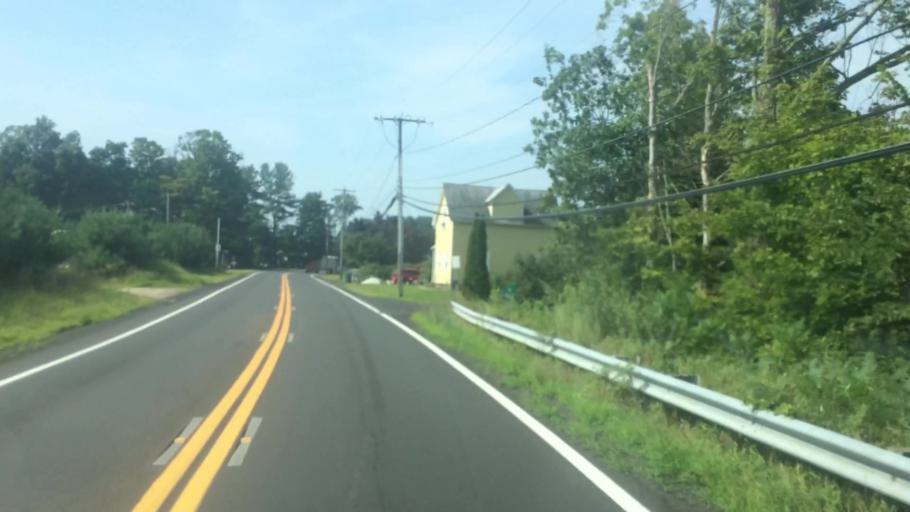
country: US
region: Massachusetts
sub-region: Hampshire County
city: Easthampton
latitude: 42.2560
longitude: -72.6915
